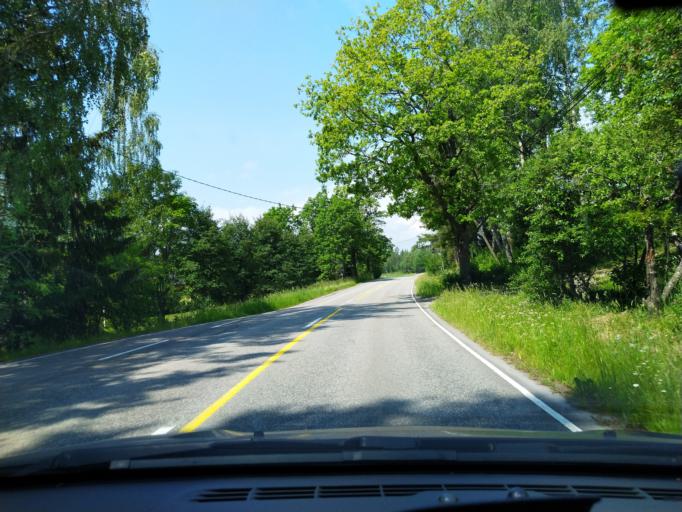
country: FI
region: Uusimaa
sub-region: Helsinki
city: Lohja
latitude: 60.3100
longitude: 24.0865
